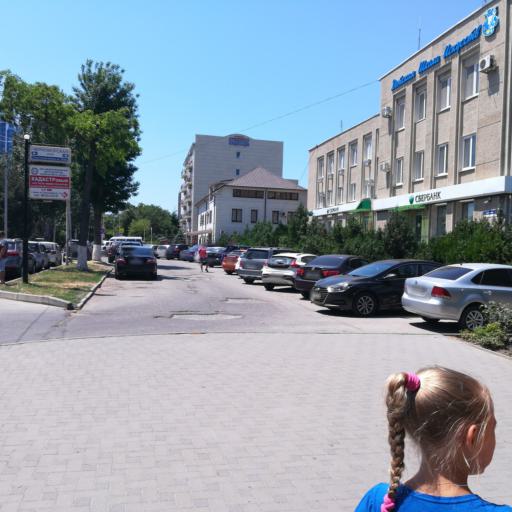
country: RU
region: Krasnodarskiy
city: Anapa
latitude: 44.8941
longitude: 37.3082
